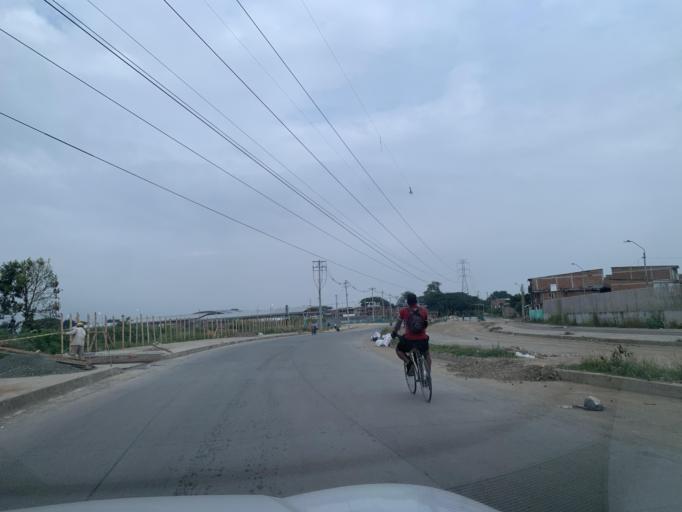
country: CO
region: Valle del Cauca
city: Cali
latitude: 3.4111
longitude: -76.4799
